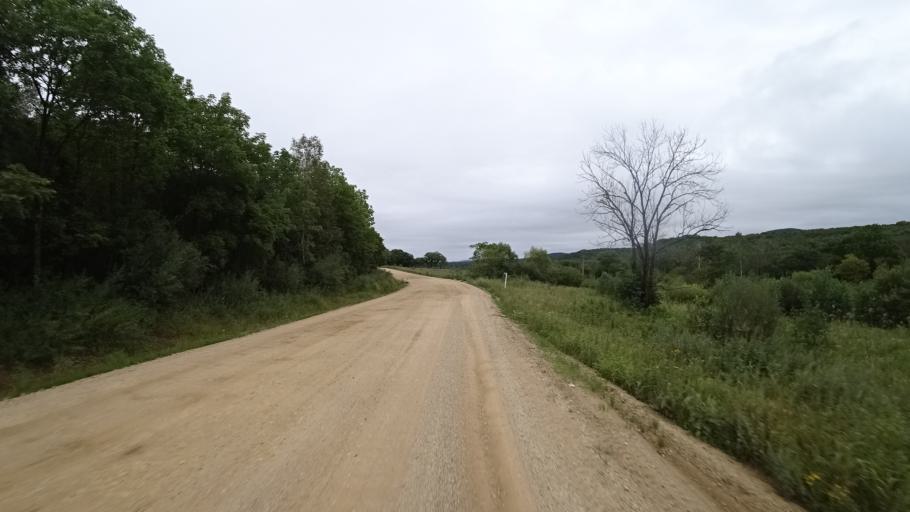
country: RU
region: Primorskiy
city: Rettikhovka
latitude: 44.1766
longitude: 132.8294
